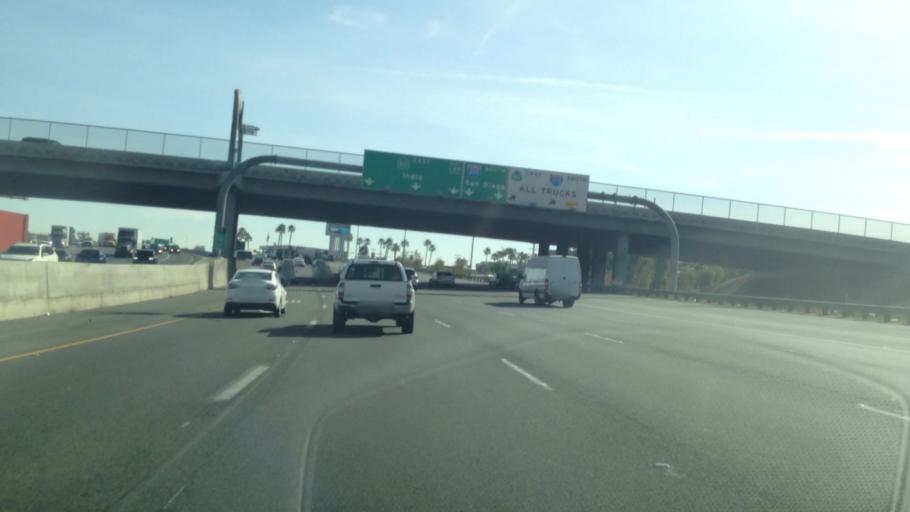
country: US
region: California
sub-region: Riverside County
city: March Air Force Base
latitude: 33.9489
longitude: -117.3022
